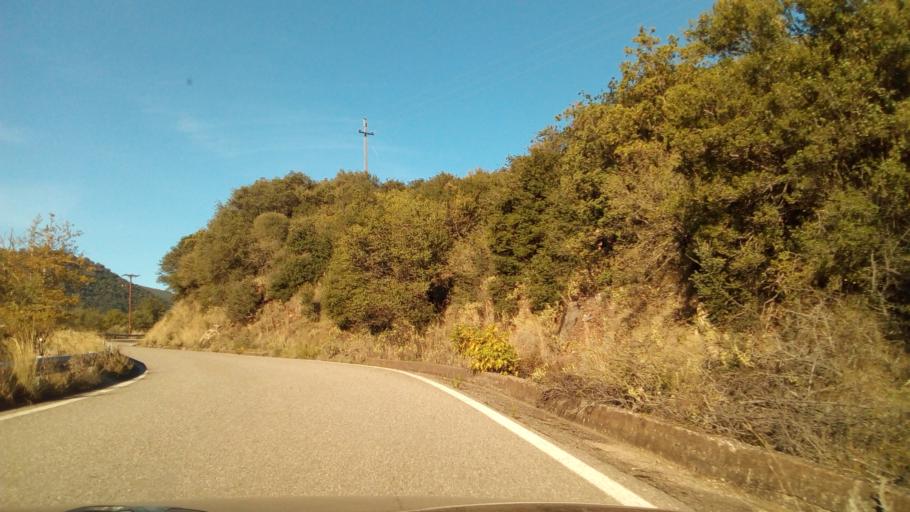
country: GR
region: West Greece
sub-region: Nomos Aitolias kai Akarnanias
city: Nafpaktos
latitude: 38.4799
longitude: 21.8671
